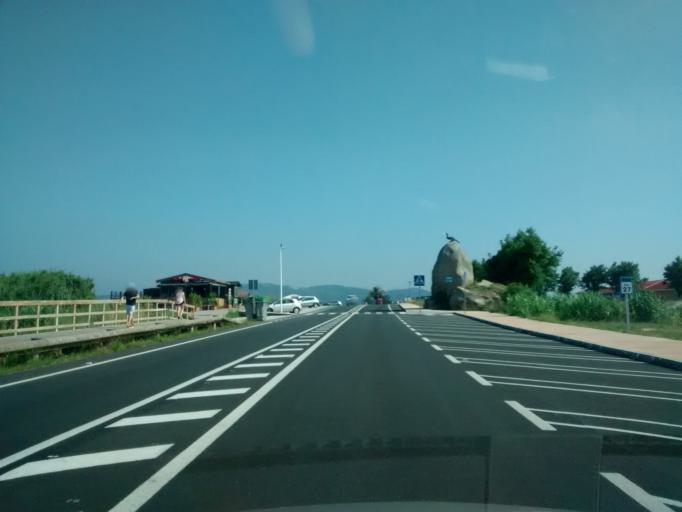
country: ES
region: Galicia
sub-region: Provincia de Pontevedra
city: O Grove
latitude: 42.4356
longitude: -8.8705
